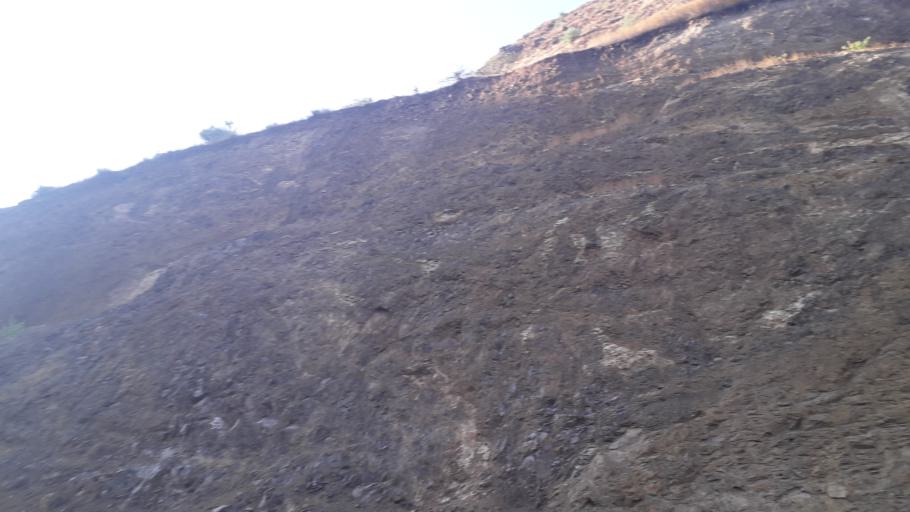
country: ET
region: Amhara
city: Dese
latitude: 11.5211
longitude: 39.2508
